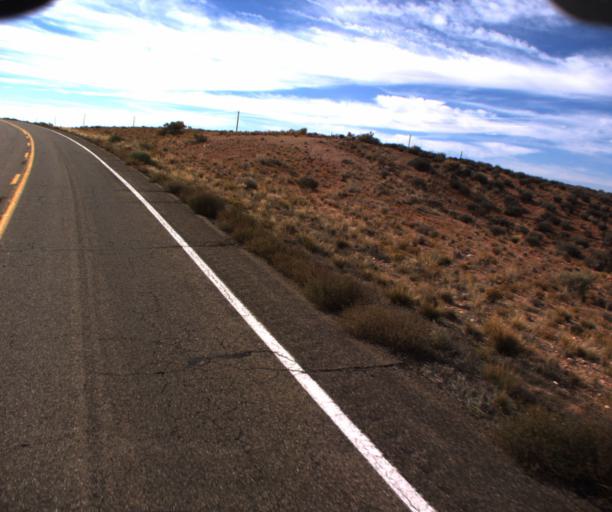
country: US
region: Arizona
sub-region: Coconino County
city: LeChee
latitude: 36.7335
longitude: -111.2842
